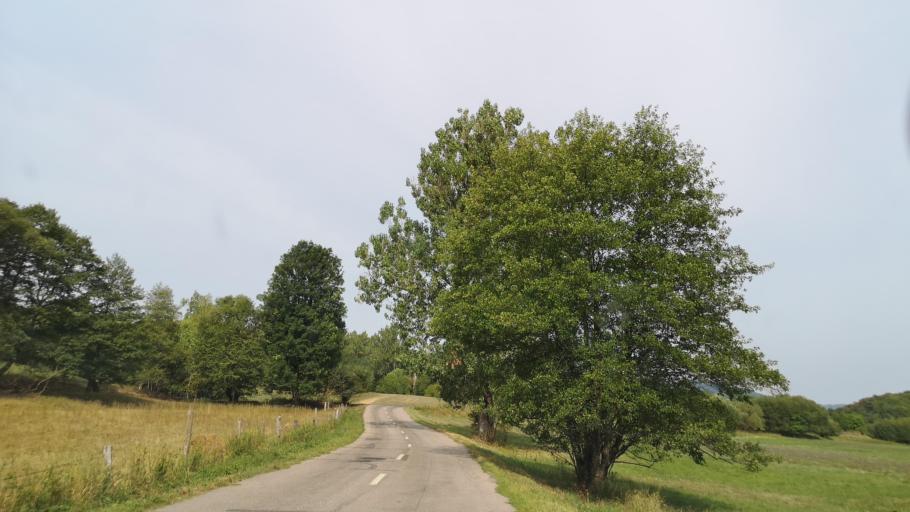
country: SK
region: Banskobystricky
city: Revuca
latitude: 48.6000
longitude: 20.0921
